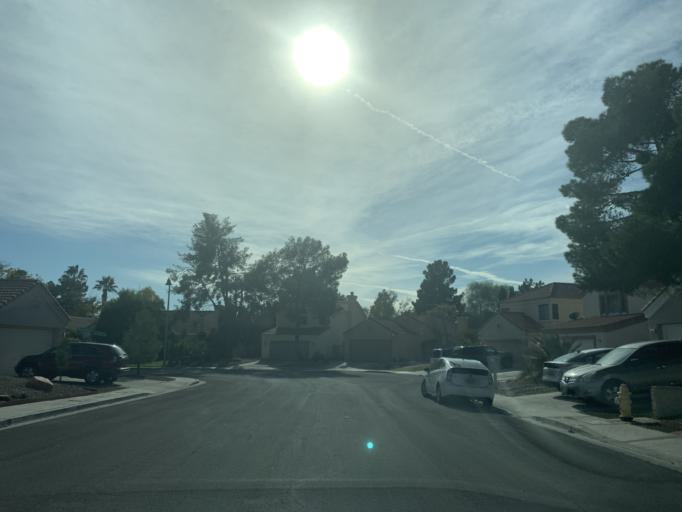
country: US
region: Nevada
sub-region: Clark County
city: Spring Valley
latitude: 36.1305
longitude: -115.2849
